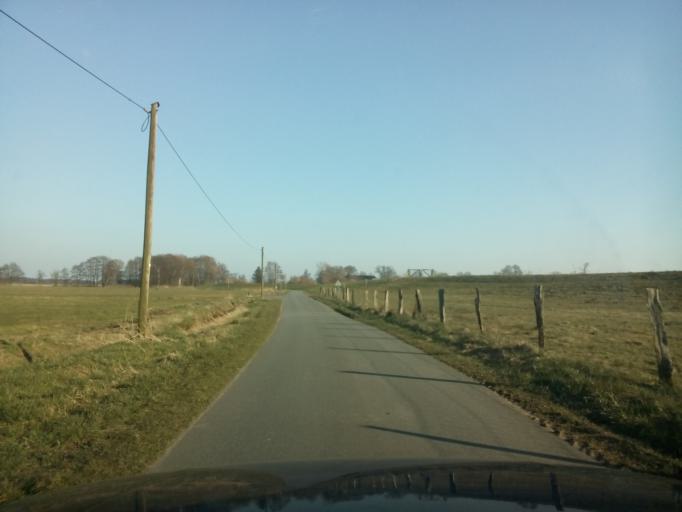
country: DE
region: Lower Saxony
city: Osterholz-Scharmbeck
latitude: 53.1592
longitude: 8.8344
